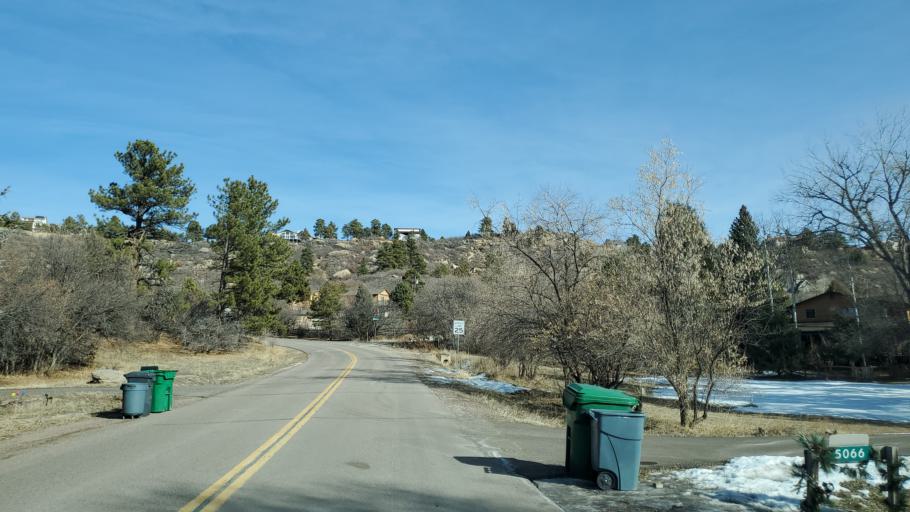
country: US
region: Colorado
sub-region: Douglas County
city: Castle Pines
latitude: 39.4334
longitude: -104.8697
